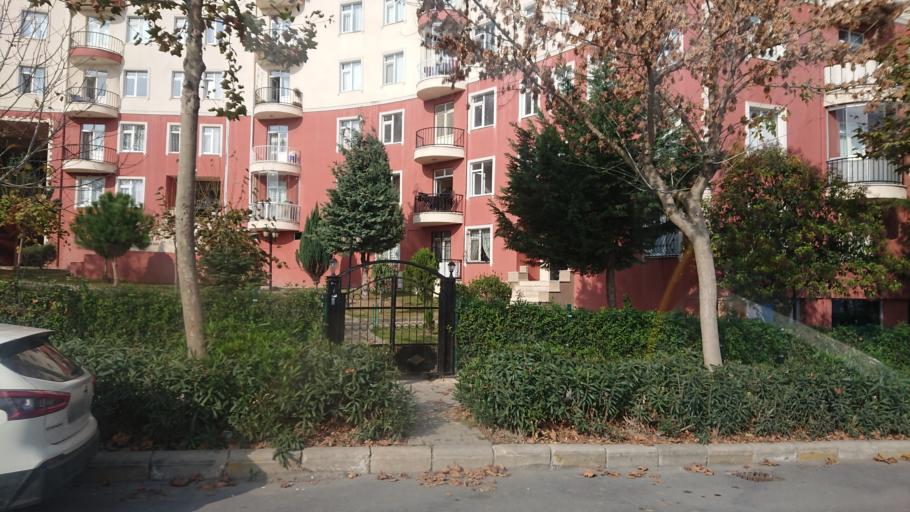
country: TR
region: Istanbul
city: Esenyurt
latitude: 41.0742
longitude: 28.6678
